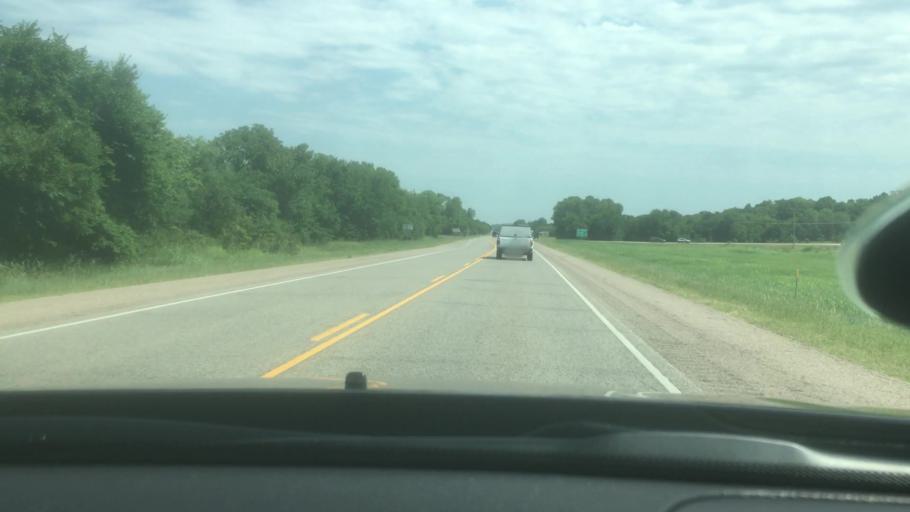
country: US
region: Oklahoma
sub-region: Seminole County
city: Maud
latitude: 35.0700
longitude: -96.9312
